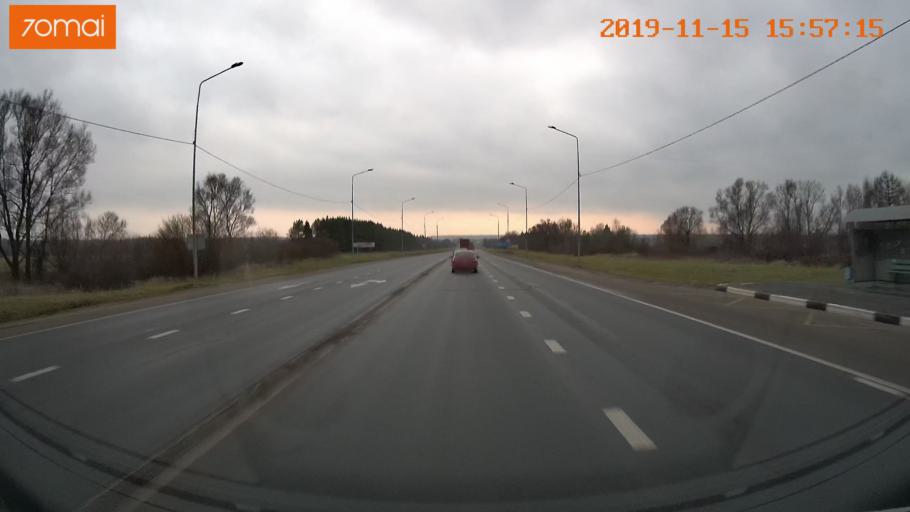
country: RU
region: Jaroslavl
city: Yaroslavl
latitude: 57.8323
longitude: 39.9653
